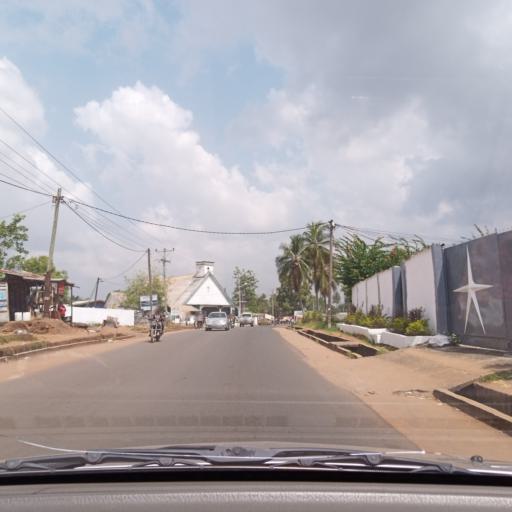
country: LR
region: Montserrado
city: Monrovia
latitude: 6.2736
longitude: -10.6956
